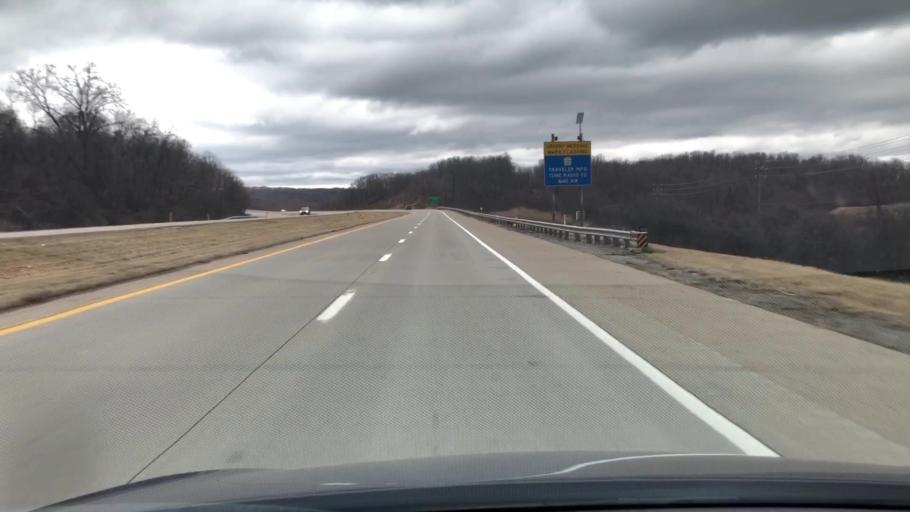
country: US
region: Pennsylvania
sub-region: Westmoreland County
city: New Stanton
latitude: 40.1918
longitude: -79.5705
